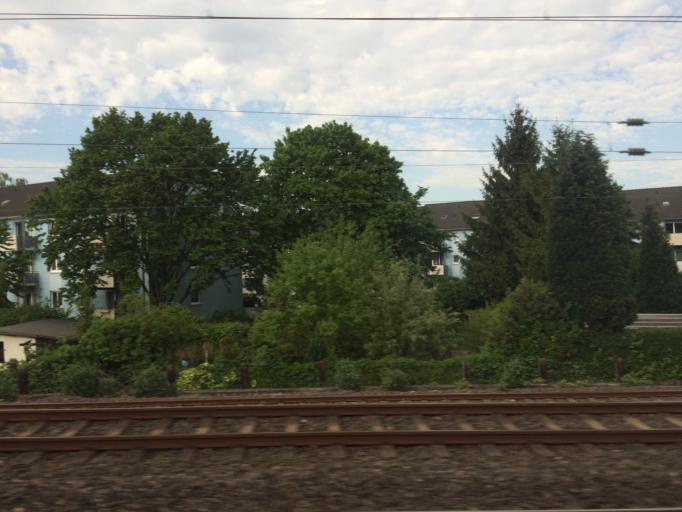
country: DE
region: North Rhine-Westphalia
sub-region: Regierungsbezirk Koln
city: Kalk
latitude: 50.9258
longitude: 7.0192
